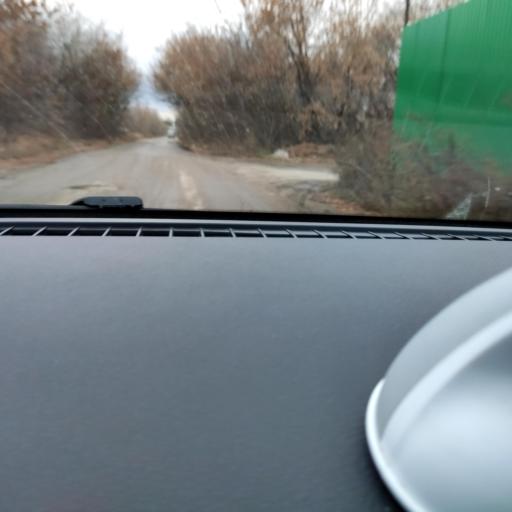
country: RU
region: Samara
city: Petra-Dubrava
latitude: 53.2612
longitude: 50.2982
